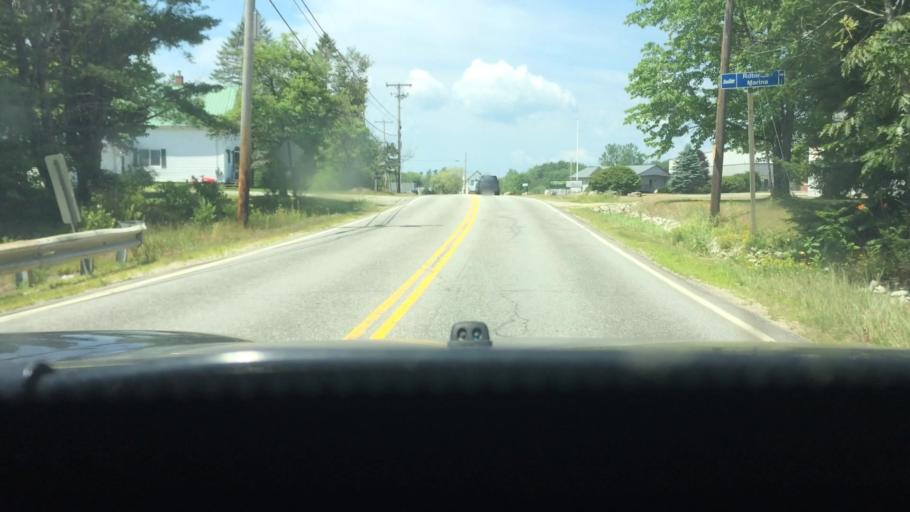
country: US
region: Maine
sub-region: Oxford County
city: Oxford
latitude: 44.1347
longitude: -70.4565
